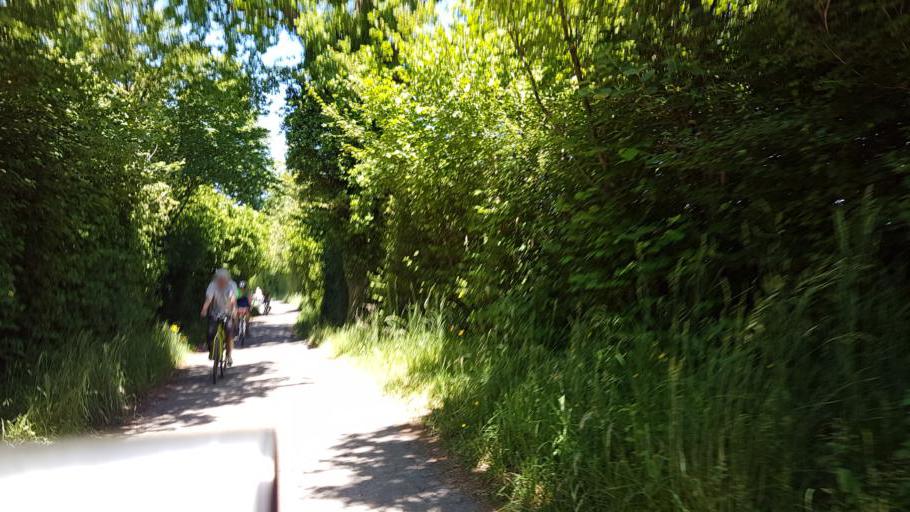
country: CH
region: Bern
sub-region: Thun District
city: Thierachern
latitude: 46.7359
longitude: 7.5663
